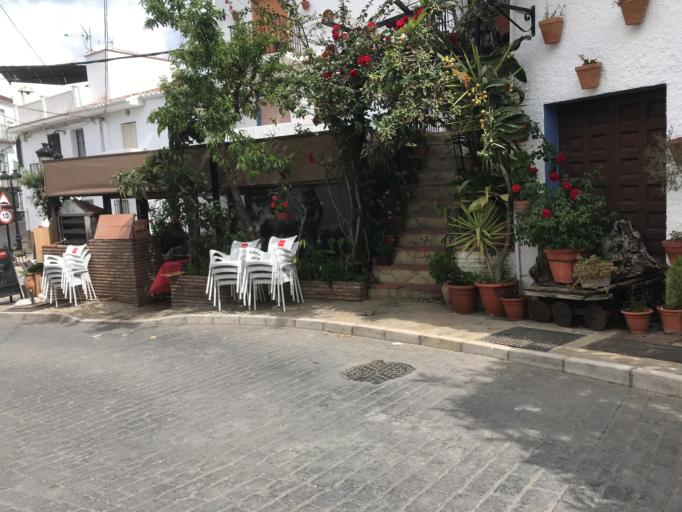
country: ES
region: Andalusia
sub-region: Provincia de Malaga
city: Alcaucin
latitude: 36.9018
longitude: -4.1136
